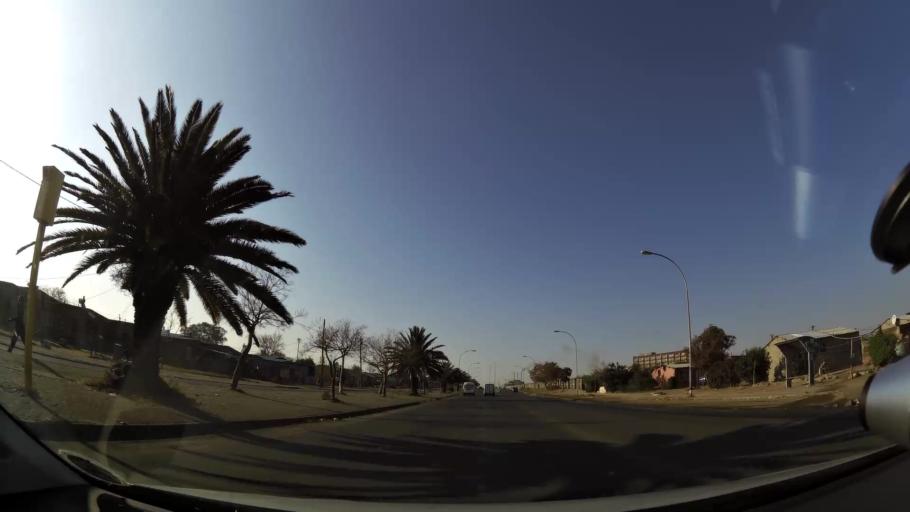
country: ZA
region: Orange Free State
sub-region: Mangaung Metropolitan Municipality
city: Bloemfontein
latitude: -29.1367
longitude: 26.2419
